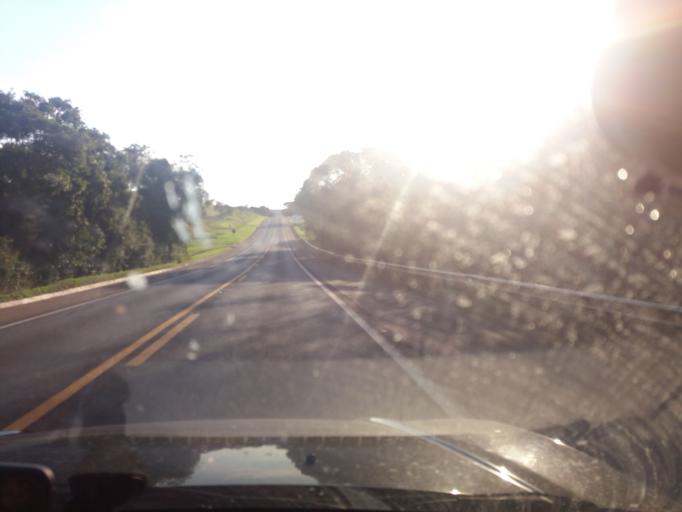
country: BR
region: Sao Paulo
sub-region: Buri
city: Buri
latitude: -23.9312
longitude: -48.6417
